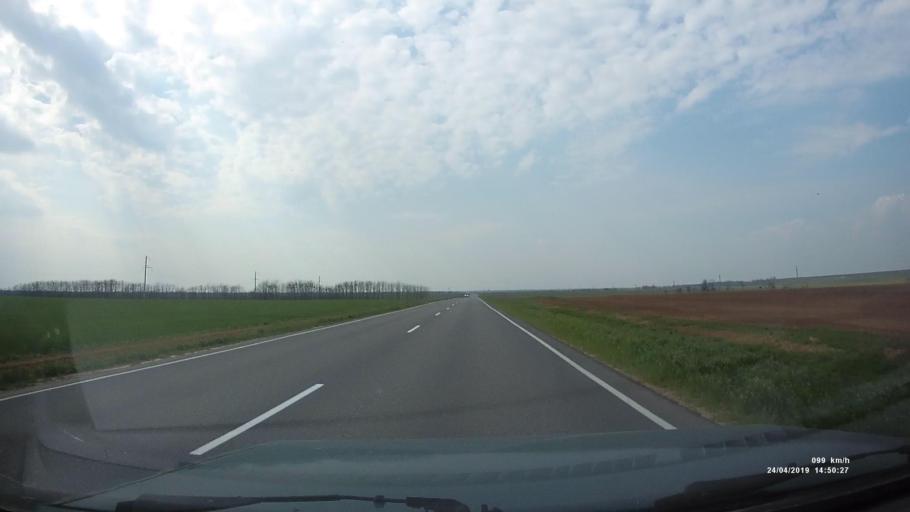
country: RU
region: Rostov
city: Remontnoye
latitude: 46.5174
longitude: 43.7191
